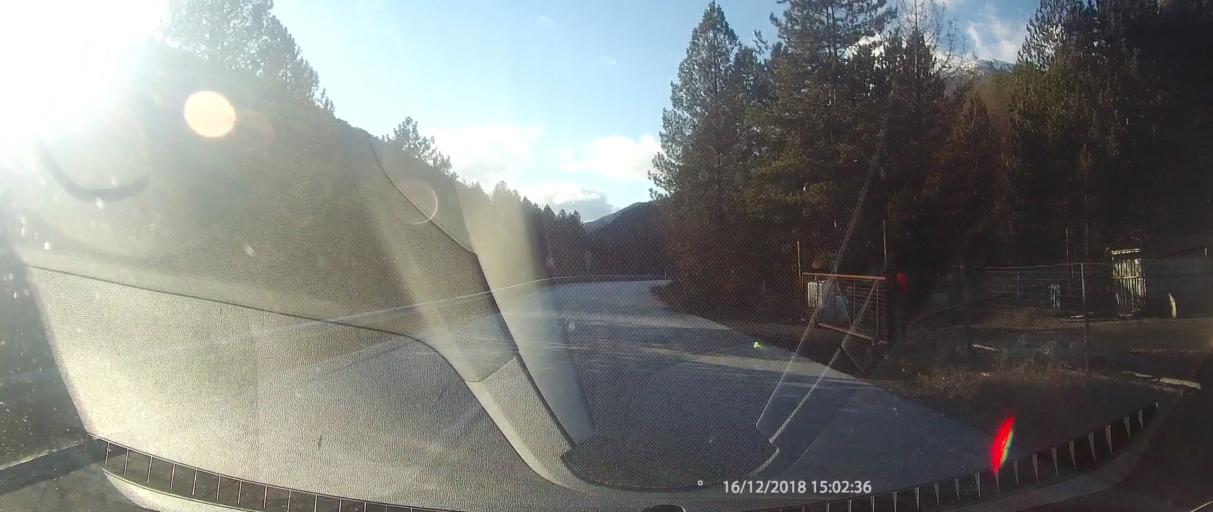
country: GR
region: West Macedonia
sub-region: Nomos Kastorias
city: Nestorio
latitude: 40.2291
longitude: 20.9933
